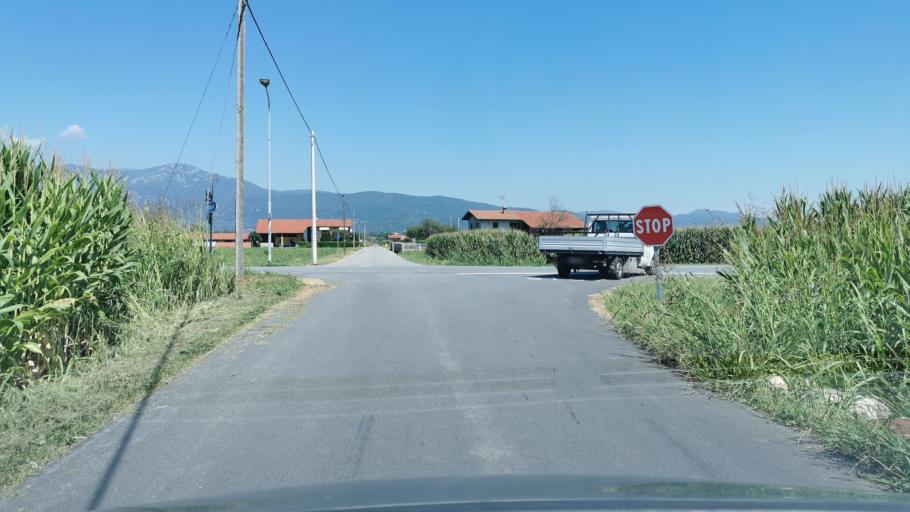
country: IT
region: Piedmont
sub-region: Provincia di Cuneo
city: Caraglio
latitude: 44.4278
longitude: 7.4351
